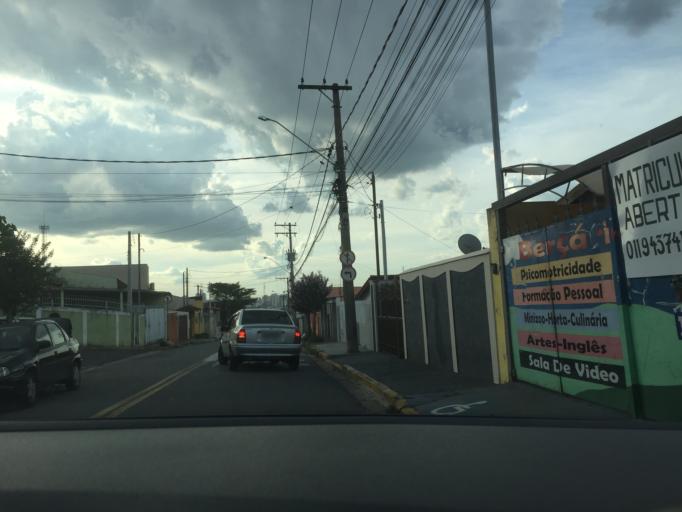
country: BR
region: Sao Paulo
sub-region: Varzea Paulista
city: Varzea Paulista
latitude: -23.2074
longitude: -46.8480
